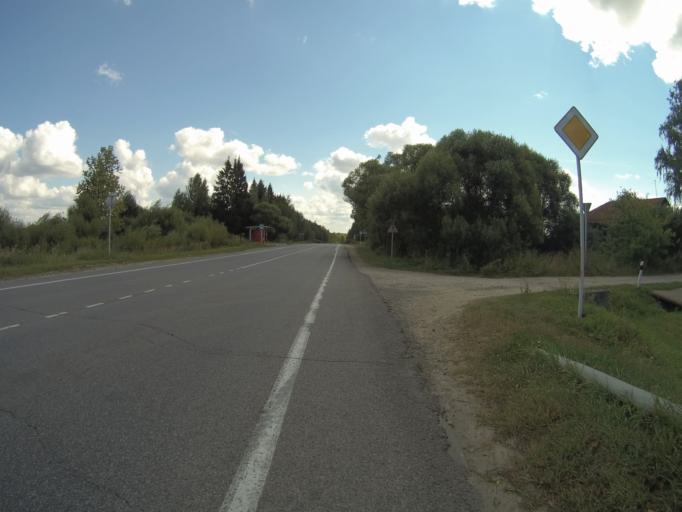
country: RU
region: Vladimir
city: Golovino
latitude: 55.9293
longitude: 40.5957
